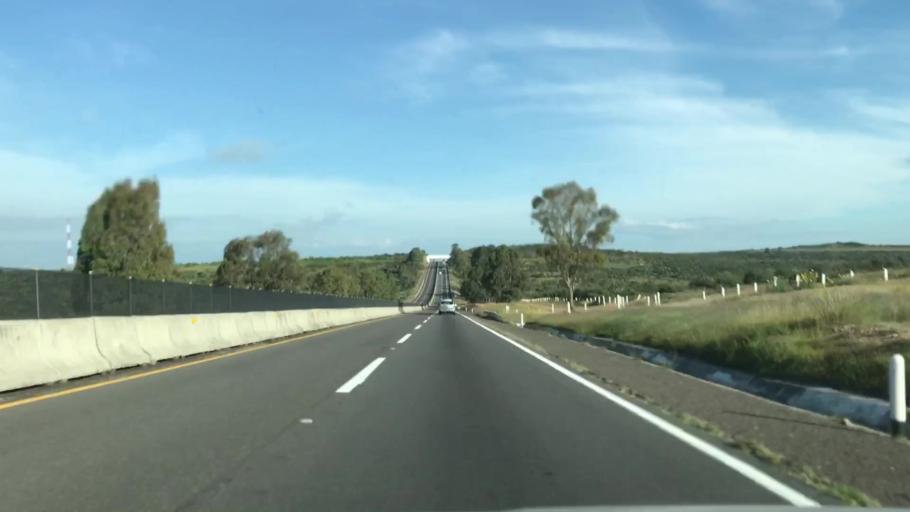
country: MX
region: Jalisco
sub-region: Lagos de Moreno
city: Cristeros [Fraccionamiento]
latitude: 21.3753
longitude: -102.1355
